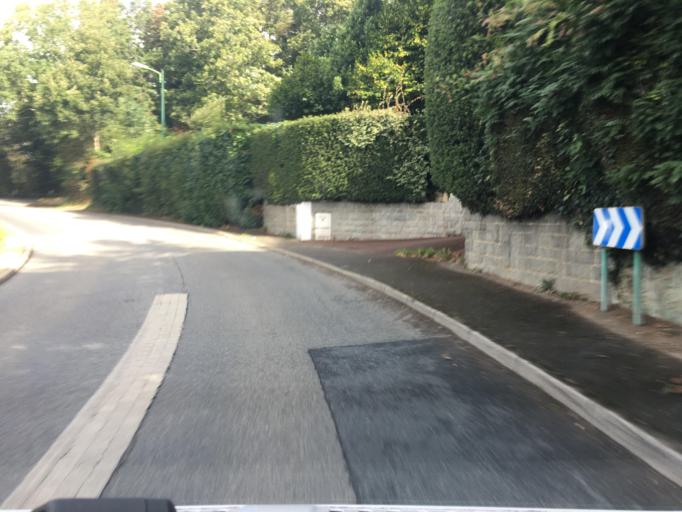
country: FR
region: Brittany
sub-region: Departement du Finistere
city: La Foret-Fouesnant
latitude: 47.9141
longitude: -3.9737
